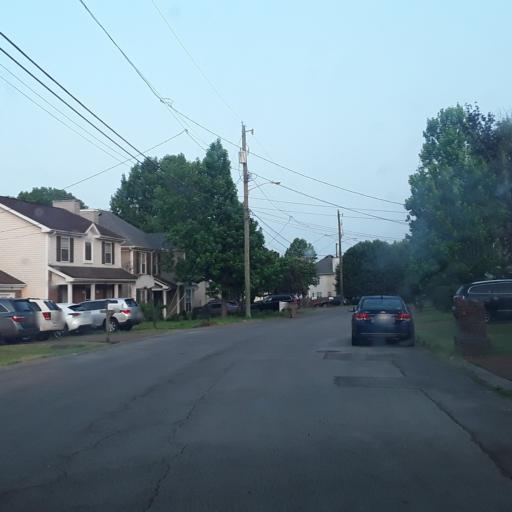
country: US
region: Tennessee
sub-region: Williamson County
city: Brentwood Estates
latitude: 36.0455
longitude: -86.7353
